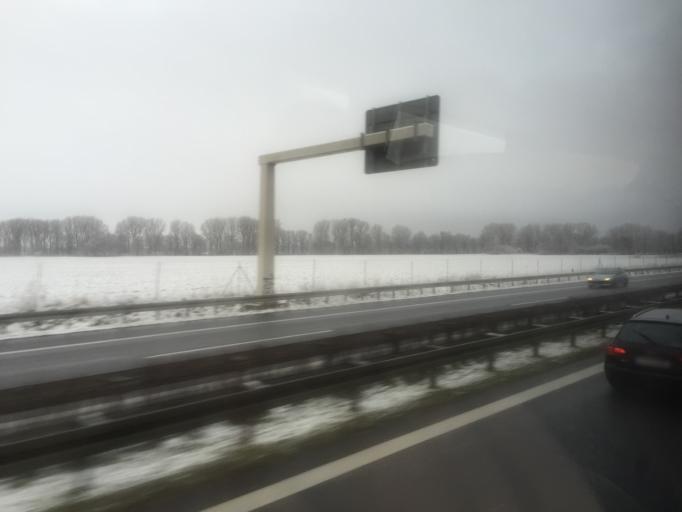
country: DE
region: Brandenburg
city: Mittenwalde
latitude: 52.2743
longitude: 13.5712
